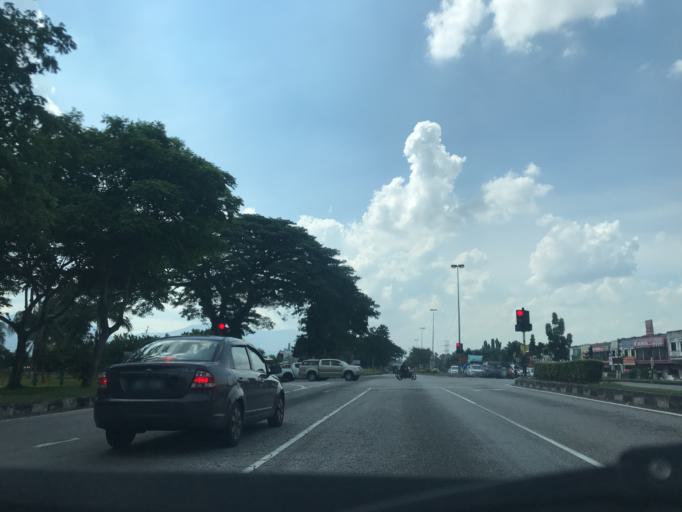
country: MY
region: Perak
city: Ipoh
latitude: 4.6308
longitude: 101.1149
